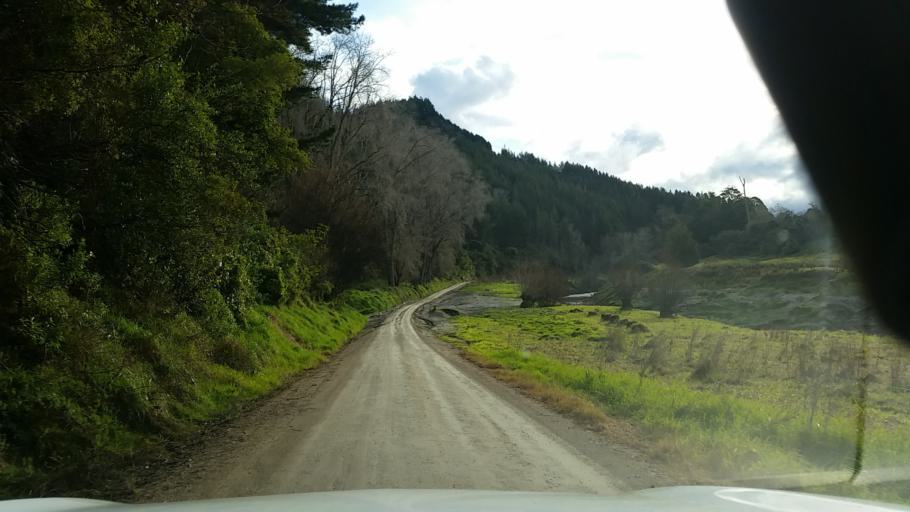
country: NZ
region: Taranaki
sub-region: South Taranaki District
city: Patea
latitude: -39.5810
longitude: 174.8317
